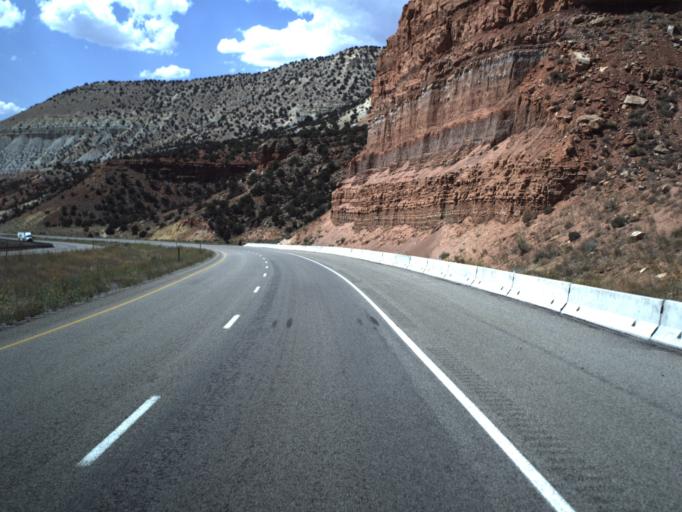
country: US
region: Utah
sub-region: Sevier County
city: Salina
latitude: 38.9310
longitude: -111.7870
